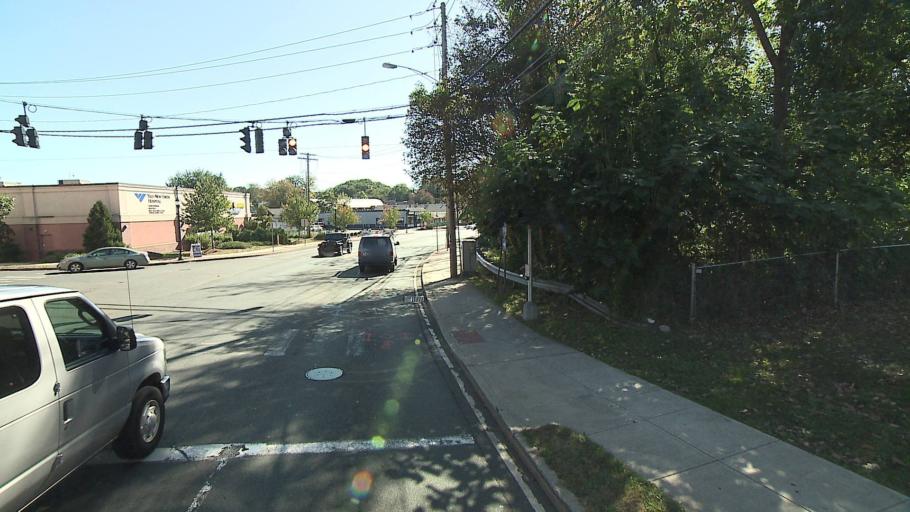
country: US
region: Connecticut
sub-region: New Haven County
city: West Haven
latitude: 41.2710
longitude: -72.9591
